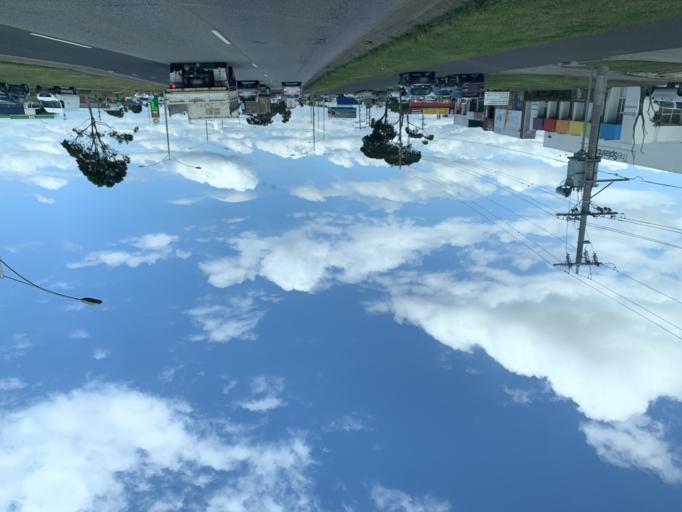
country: AU
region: Victoria
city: Heatherton
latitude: -37.9848
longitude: 145.1098
